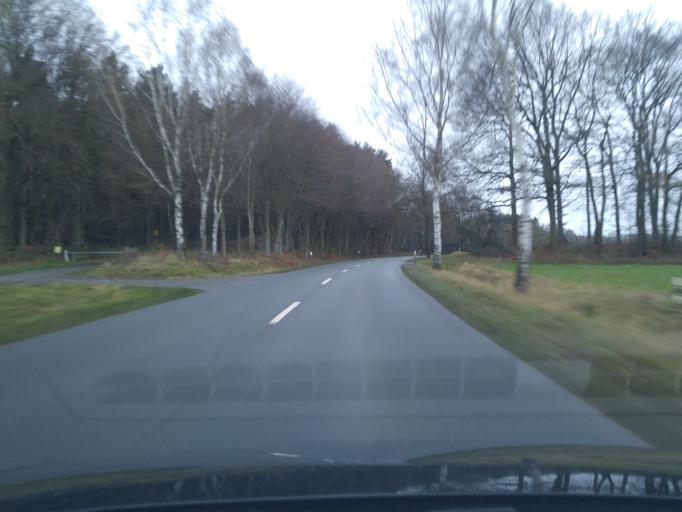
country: DE
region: Lower Saxony
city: Rullstorf
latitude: 53.2583
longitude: 10.5222
